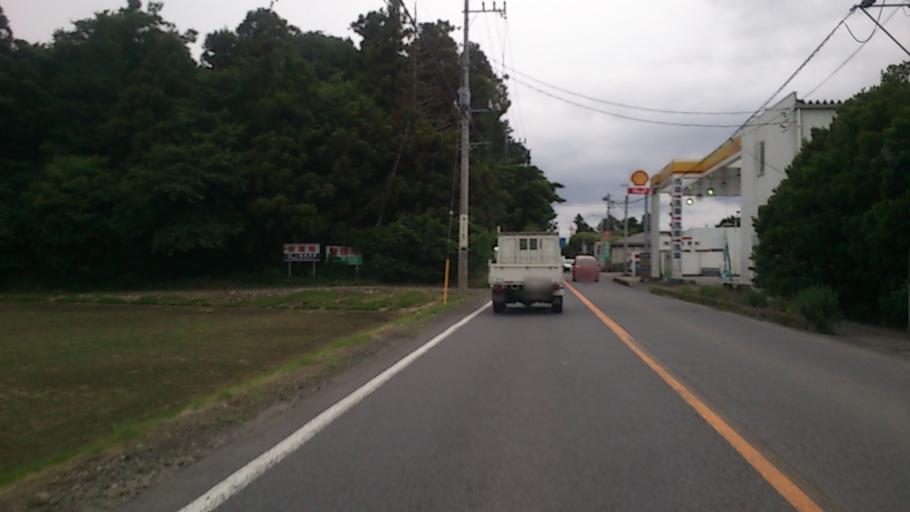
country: JP
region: Ibaraki
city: Ishige
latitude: 36.1061
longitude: 140.0418
